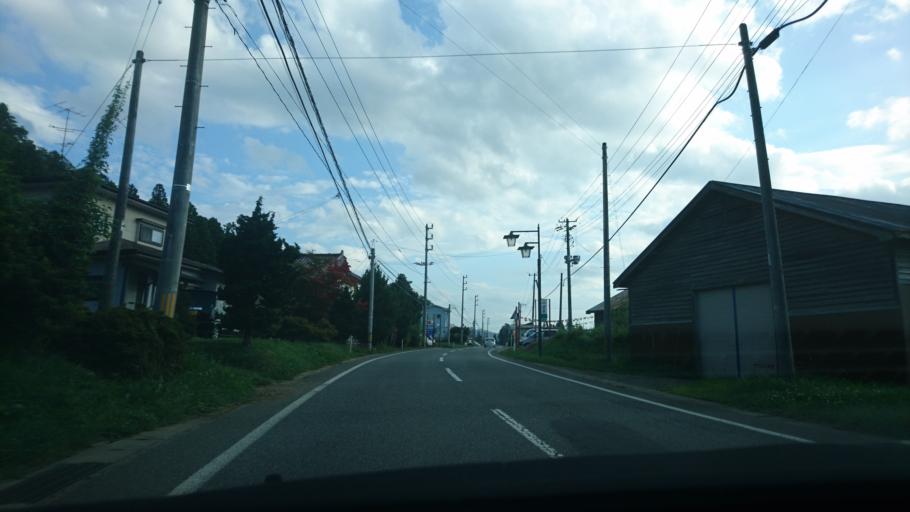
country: JP
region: Iwate
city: Mizusawa
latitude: 39.0320
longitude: 141.2954
